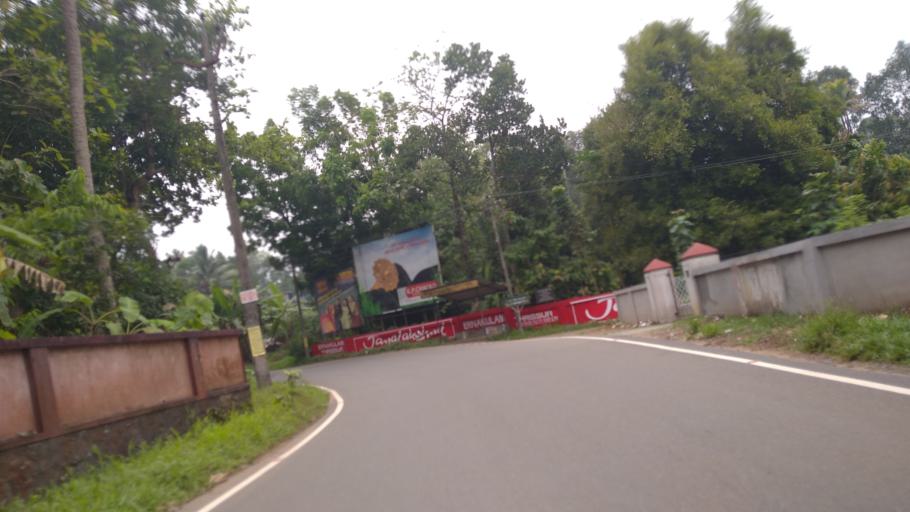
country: IN
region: Kerala
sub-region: Ernakulam
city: Perumpavur
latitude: 10.1196
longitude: 76.5325
